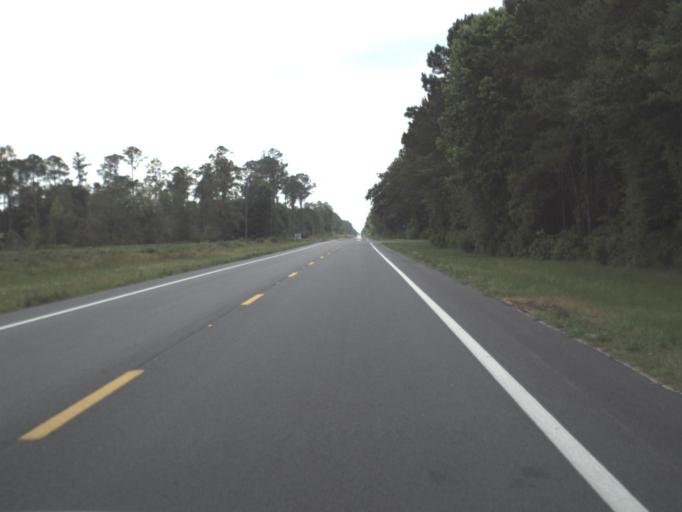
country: US
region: Florida
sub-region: Columbia County
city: Five Points
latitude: 30.3761
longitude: -82.6237
